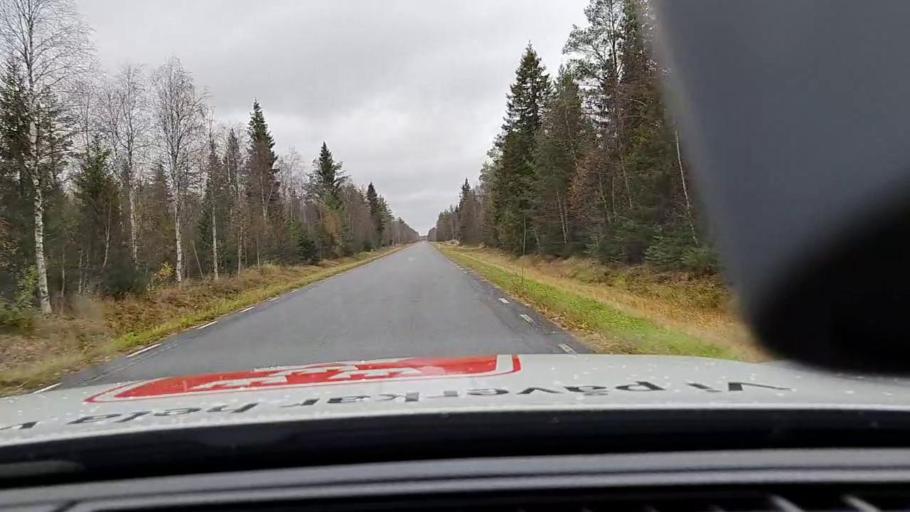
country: SE
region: Norrbotten
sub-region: Haparanda Kommun
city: Haparanda
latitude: 65.9135
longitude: 23.8277
